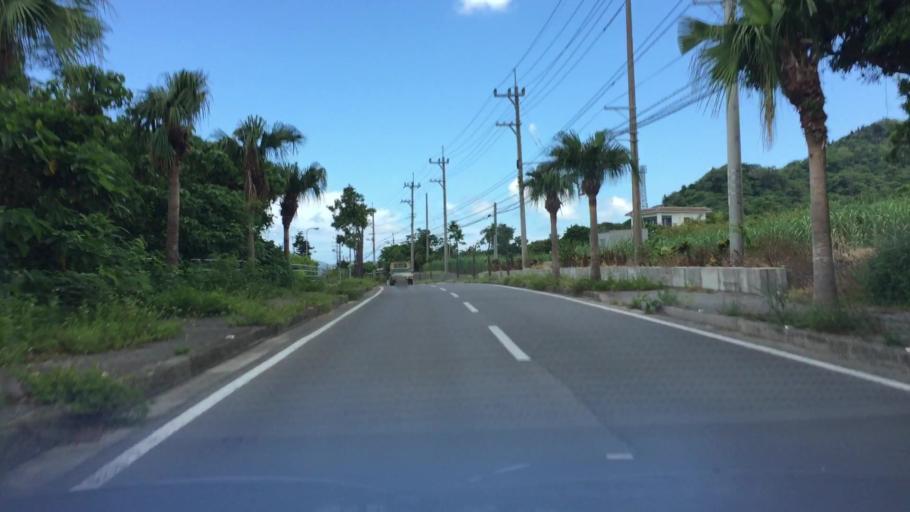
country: JP
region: Okinawa
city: Ishigaki
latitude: 24.4455
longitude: 124.1498
